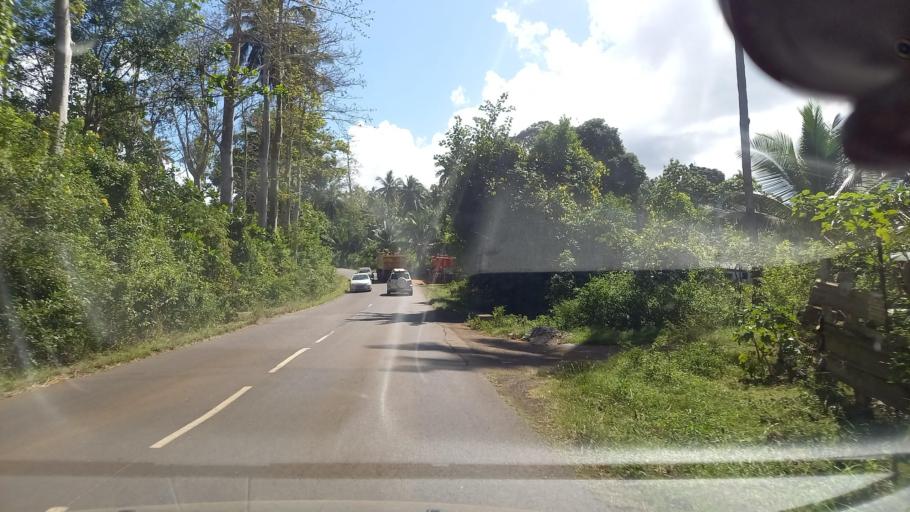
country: YT
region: M'Tsangamouji
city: M'Tsangamouji
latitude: -12.7557
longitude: 45.0953
